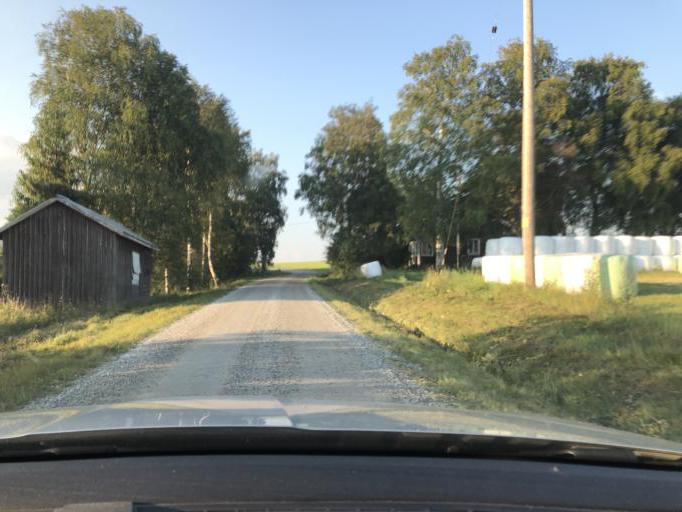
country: SE
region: Vaesternorrland
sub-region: Kramfors Kommun
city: Bollstabruk
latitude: 63.0731
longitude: 17.7360
